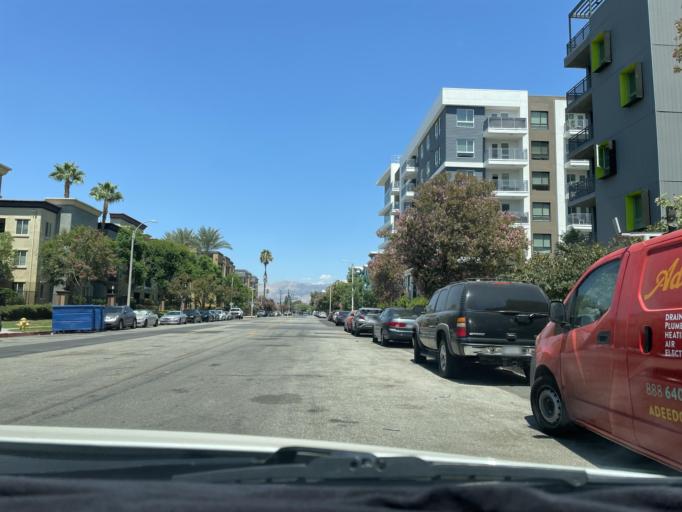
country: US
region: California
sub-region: Los Angeles County
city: Canoga Park
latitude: 34.1902
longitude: -118.5928
